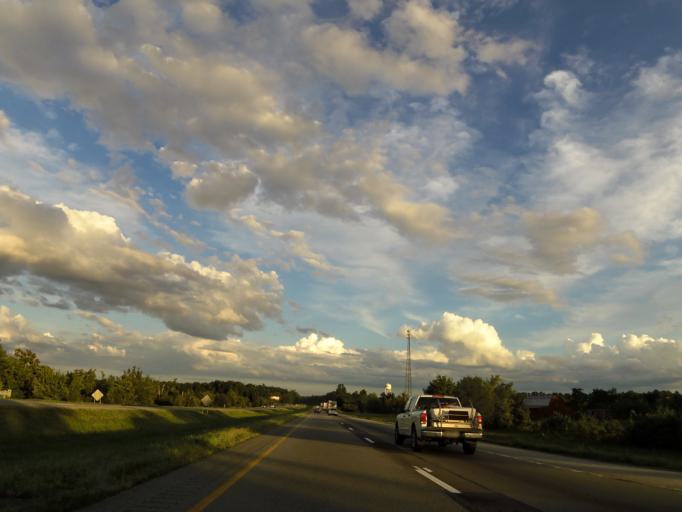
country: US
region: Tennessee
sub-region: Putnam County
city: Monterey
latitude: 36.0995
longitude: -85.2370
